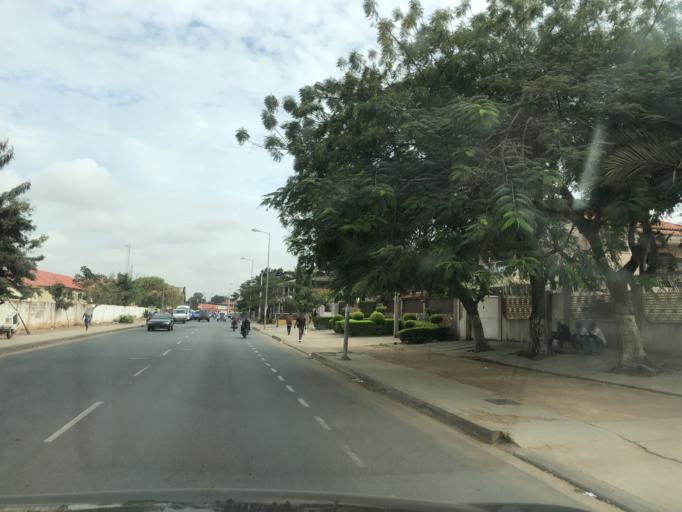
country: AO
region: Luanda
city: Luanda
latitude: -8.9141
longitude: 13.3721
